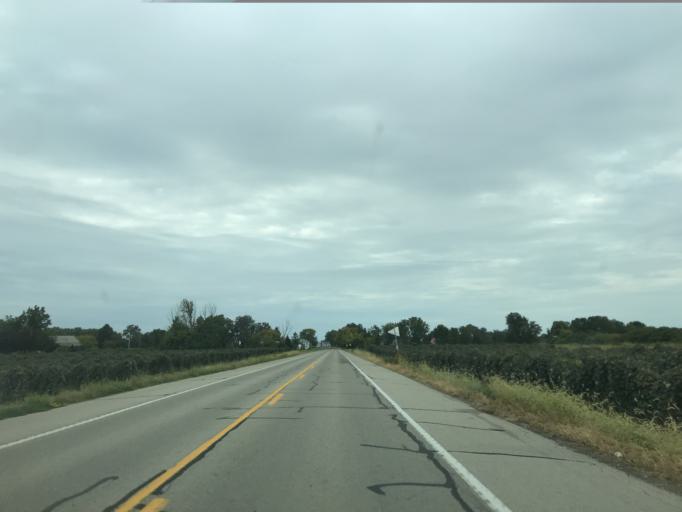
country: US
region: Pennsylvania
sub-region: Erie County
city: North East
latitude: 42.2396
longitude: -79.7671
